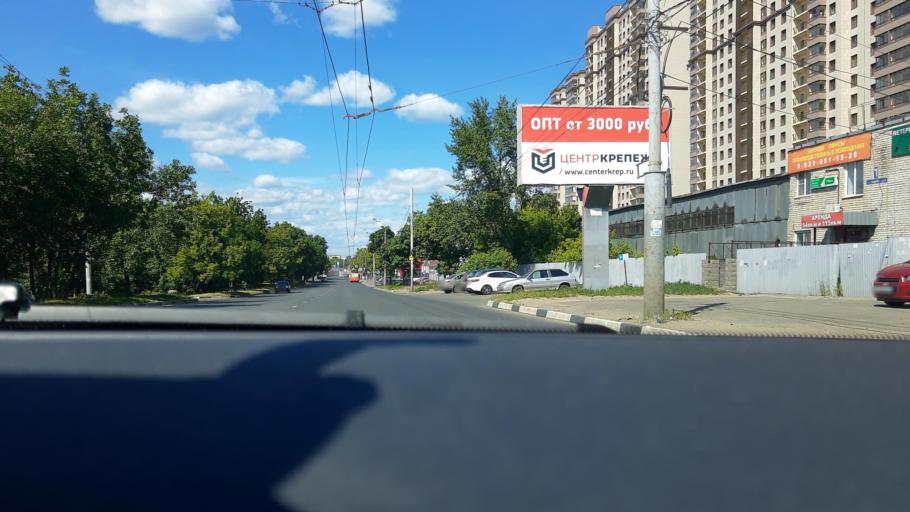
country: RU
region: Nizjnij Novgorod
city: Nizhniy Novgorod
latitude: 56.3059
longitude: 43.9451
